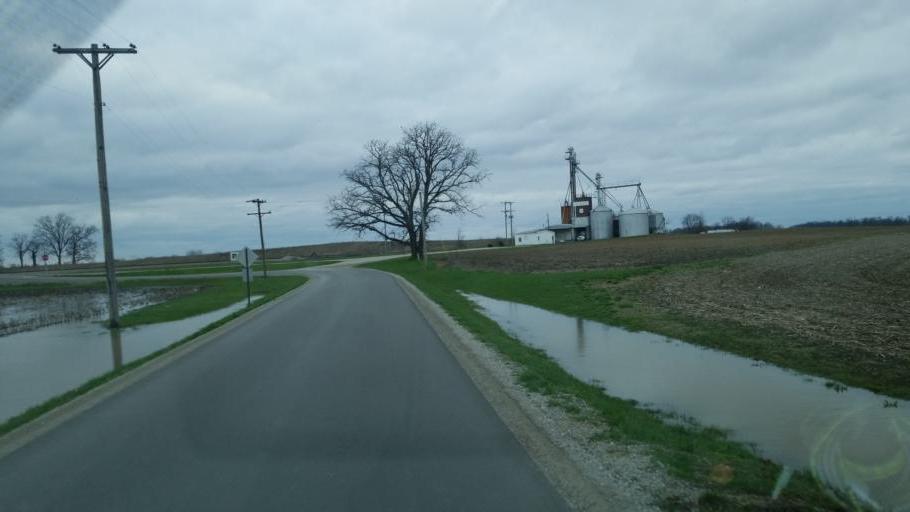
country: US
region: Ohio
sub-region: Fayette County
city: Jeffersonville
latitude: 39.5883
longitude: -83.5142
